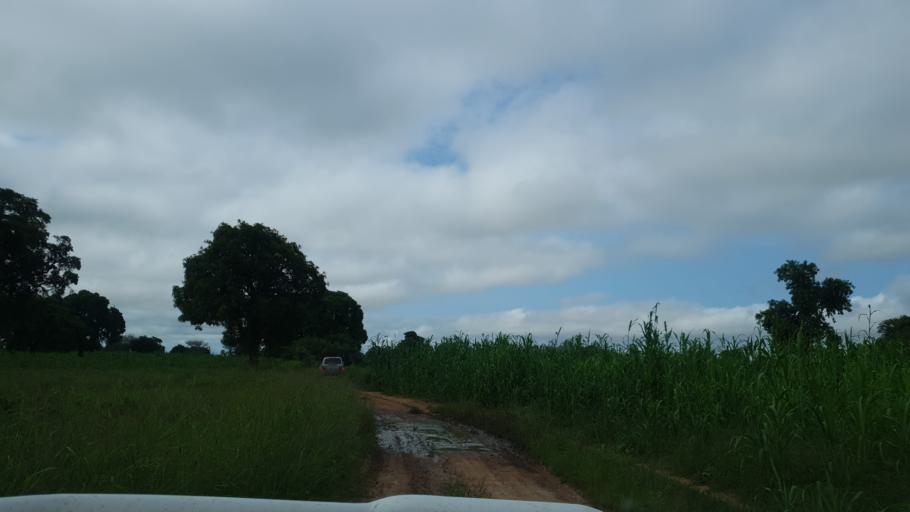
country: ML
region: Segou
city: Baroueli
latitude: 13.4919
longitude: -6.8968
